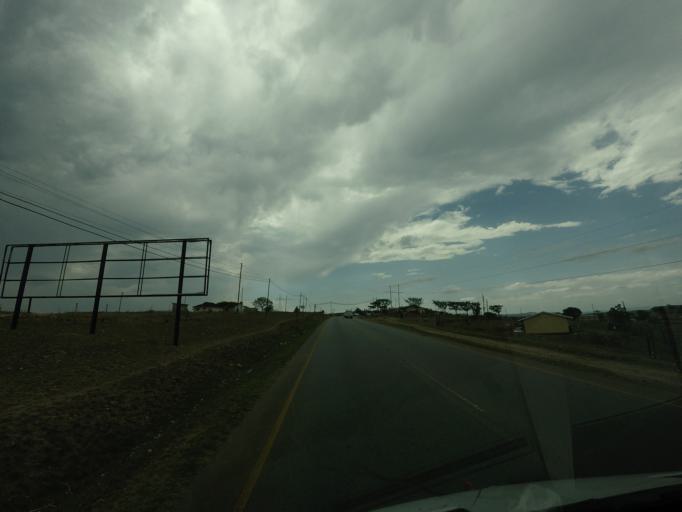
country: SZ
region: Manzini
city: Manzini
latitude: -26.5102
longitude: 31.5117
